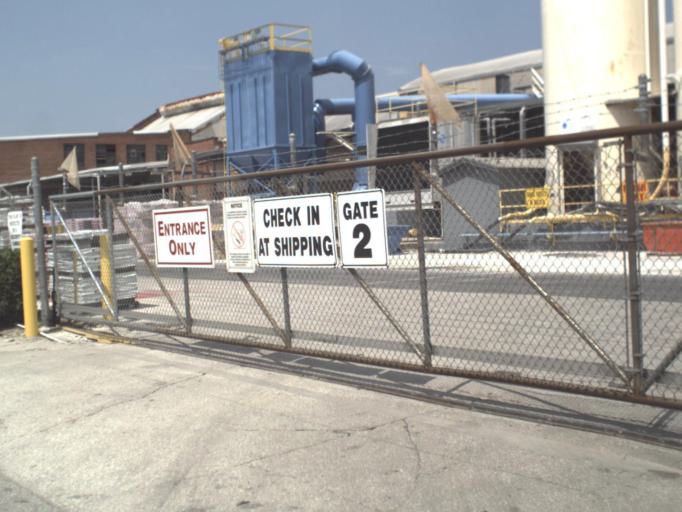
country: US
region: Florida
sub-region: Duval County
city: Jacksonville
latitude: 30.3364
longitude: -81.6307
